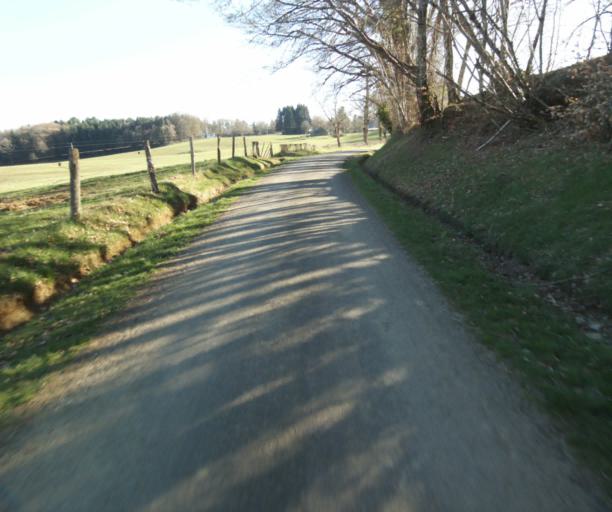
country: FR
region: Limousin
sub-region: Departement de la Correze
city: Seilhac
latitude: 45.3853
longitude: 1.6903
